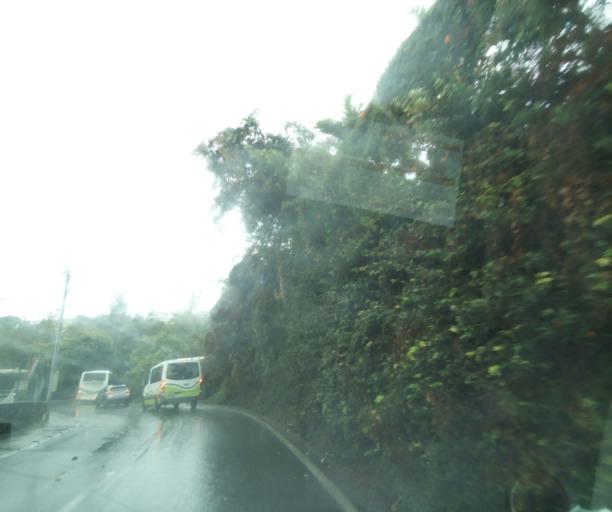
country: RE
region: Reunion
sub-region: Reunion
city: Saint-Paul
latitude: -20.9944
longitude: 55.3308
